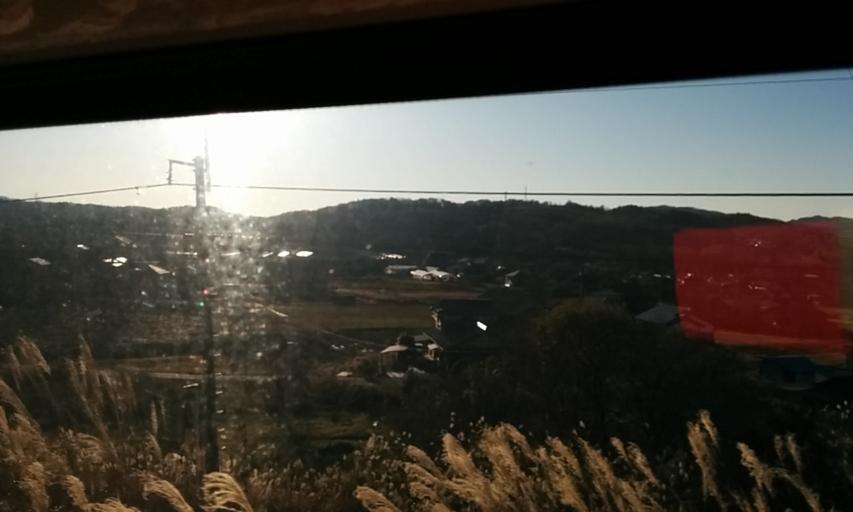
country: JP
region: Gifu
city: Nakatsugawa
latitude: 35.4630
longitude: 137.4120
